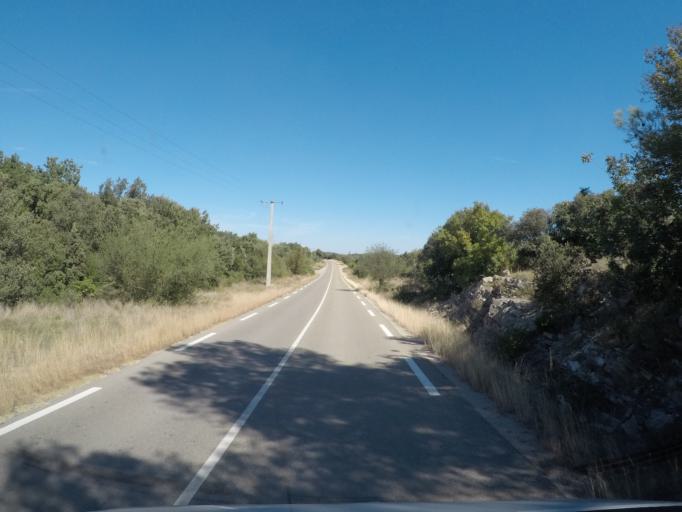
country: FR
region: Languedoc-Roussillon
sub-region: Departement de l'Herault
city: Vailhauques
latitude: 43.7332
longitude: 3.6890
